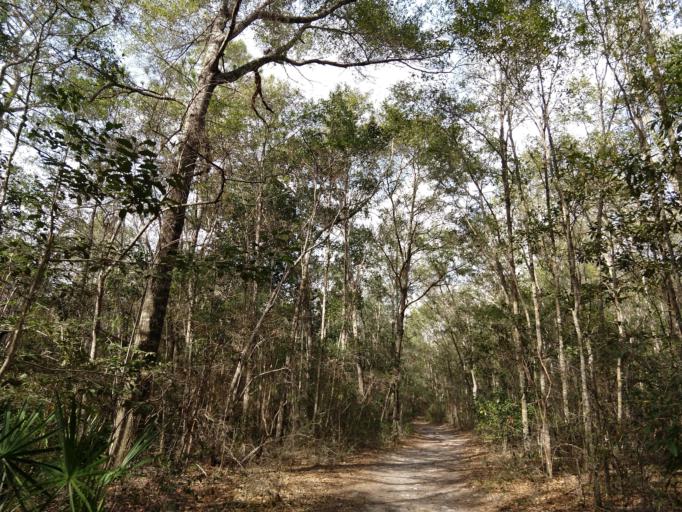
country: US
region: Florida
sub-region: Walton County
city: Seaside
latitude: 30.3727
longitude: -86.1200
